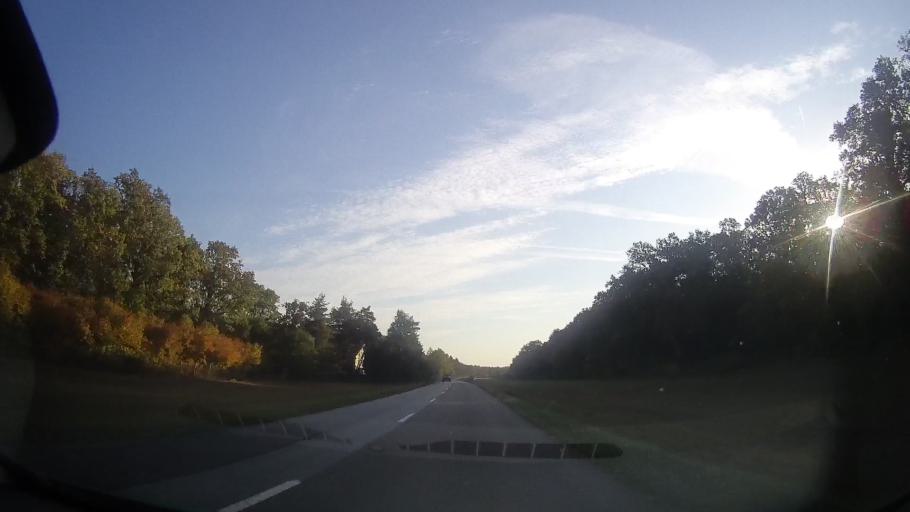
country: RO
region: Timis
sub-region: Comuna Pischia
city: Pischia
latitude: 45.9200
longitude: 21.3614
